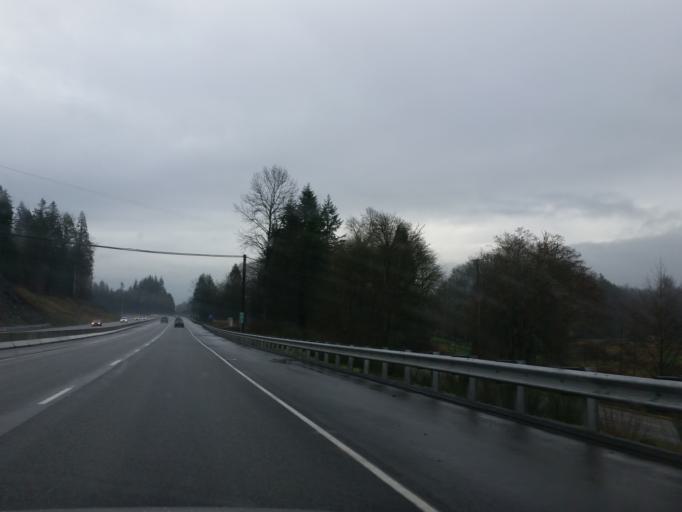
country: US
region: Washington
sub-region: Snohomish County
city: Cathcart
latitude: 47.8307
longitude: -122.0403
